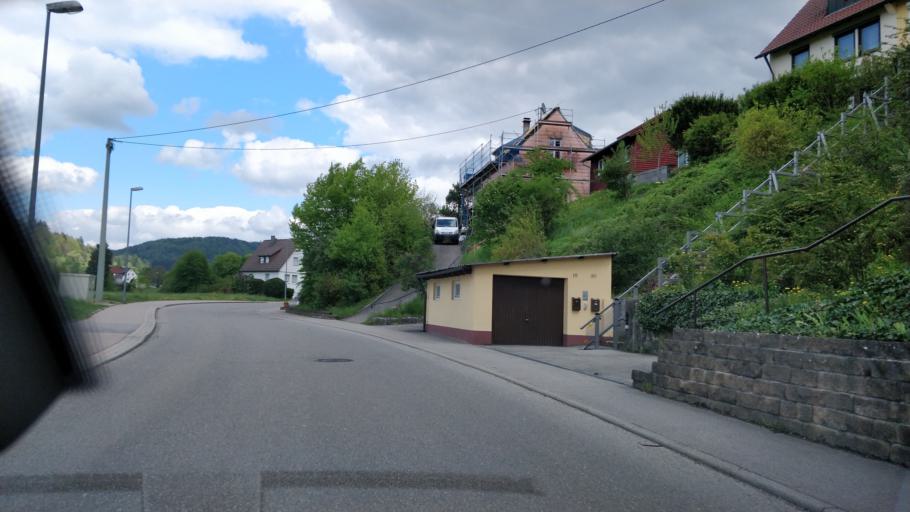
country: DE
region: Baden-Wuerttemberg
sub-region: Regierungsbezirk Stuttgart
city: Murrhardt
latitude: 48.9830
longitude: 9.5824
